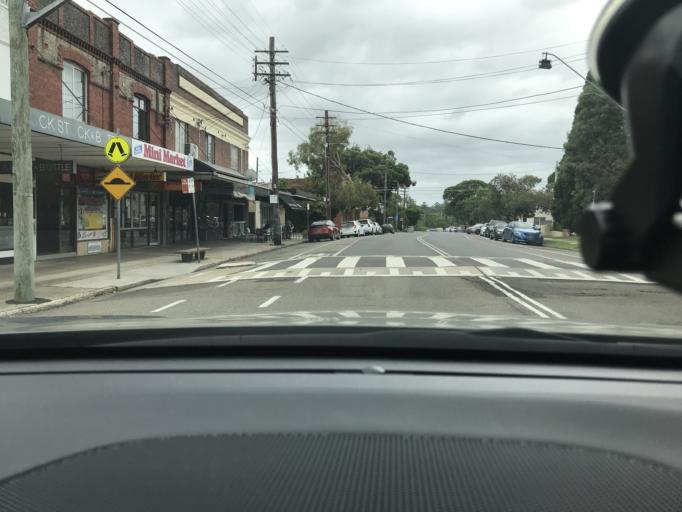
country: AU
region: New South Wales
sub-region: Canada Bay
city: Wareemba
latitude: -33.8479
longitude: 151.1282
